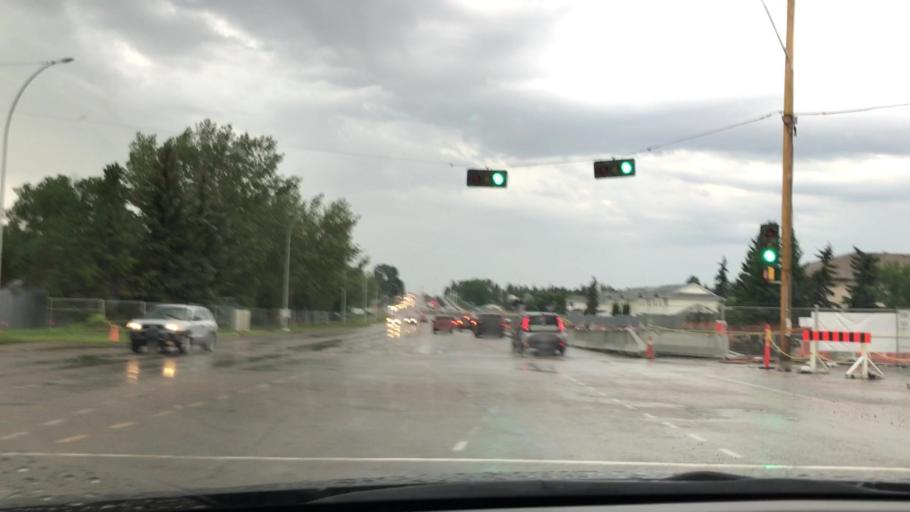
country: CA
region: Alberta
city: Edmonton
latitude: 53.4620
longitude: -113.4346
